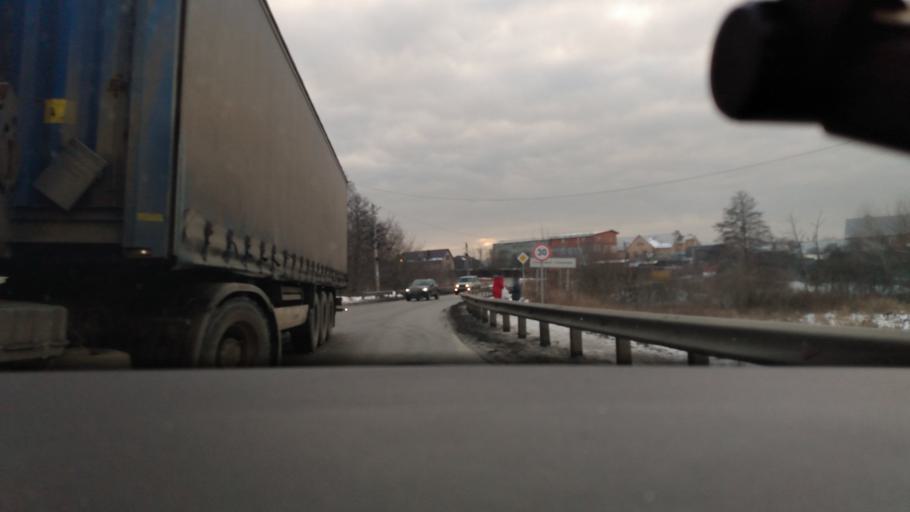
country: RU
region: Moskovskaya
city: Chornaya
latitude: 55.7087
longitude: 38.0490
